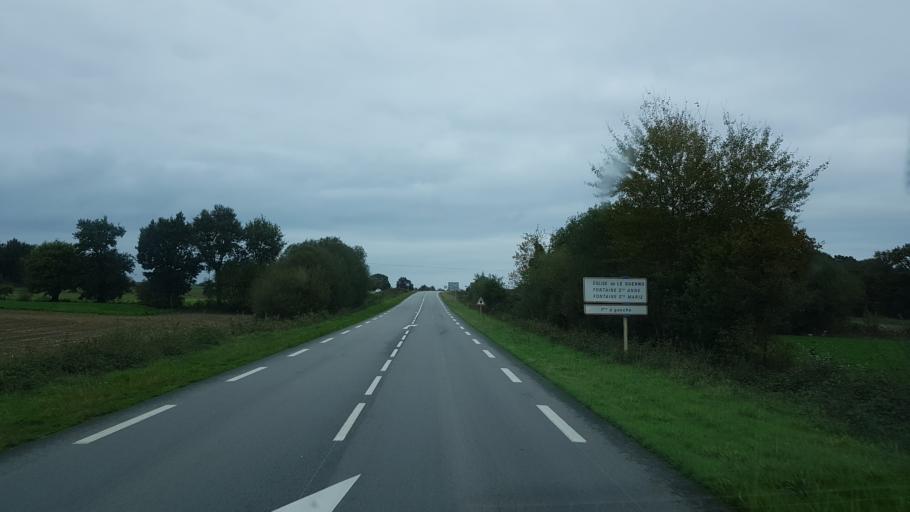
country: FR
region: Brittany
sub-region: Departement du Morbihan
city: Peaule
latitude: 47.5831
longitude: -2.3775
